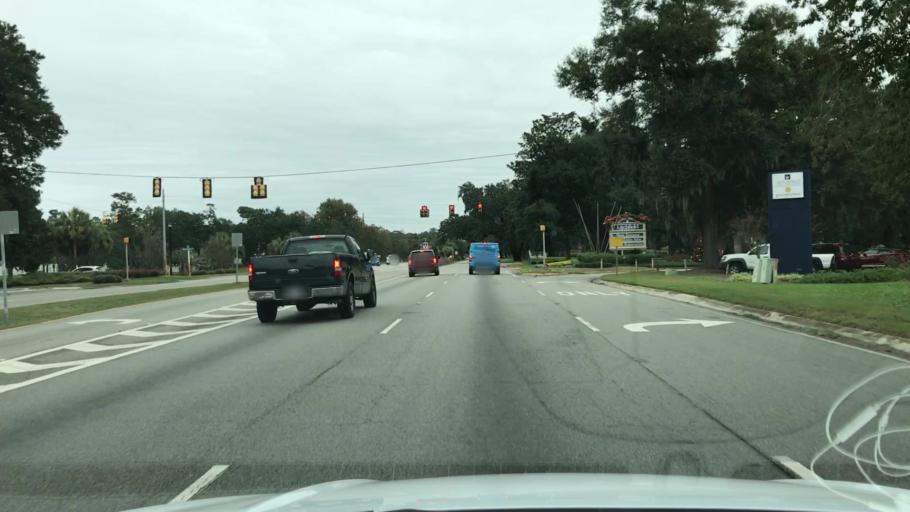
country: US
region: South Carolina
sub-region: Georgetown County
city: Murrells Inlet
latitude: 33.4831
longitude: -79.0967
